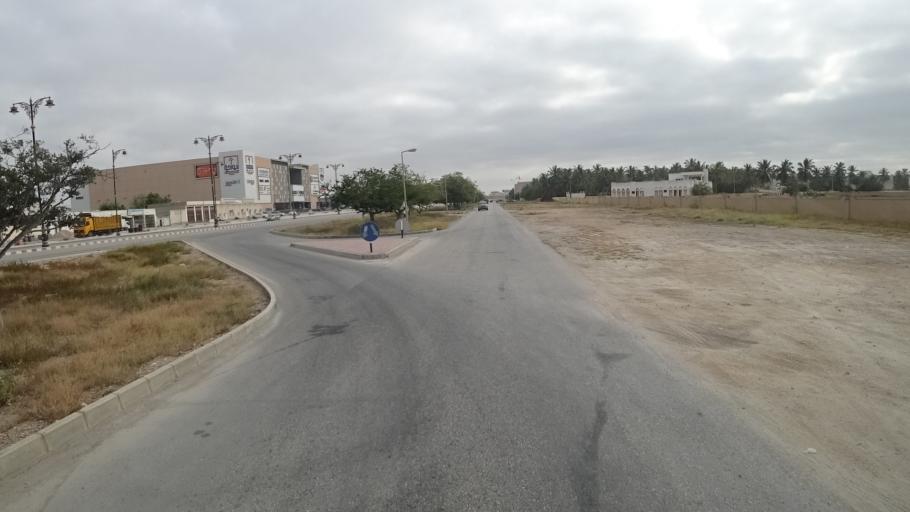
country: OM
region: Zufar
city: Salalah
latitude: 17.0121
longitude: 54.0493
